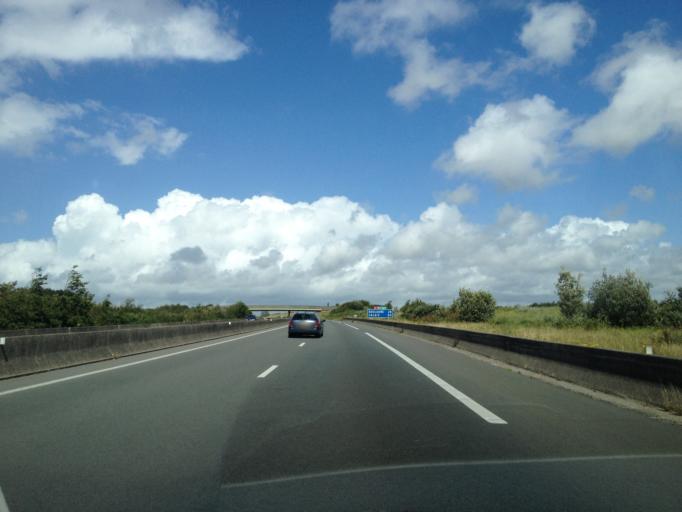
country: FR
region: Nord-Pas-de-Calais
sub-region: Departement du Pas-de-Calais
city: Etaples
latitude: 50.5177
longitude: 1.6868
